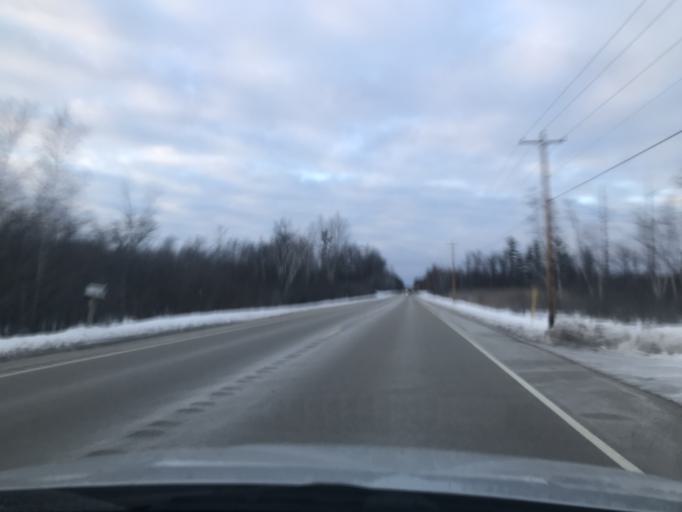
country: US
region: Wisconsin
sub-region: Marinette County
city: Marinette
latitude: 45.1223
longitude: -87.6834
